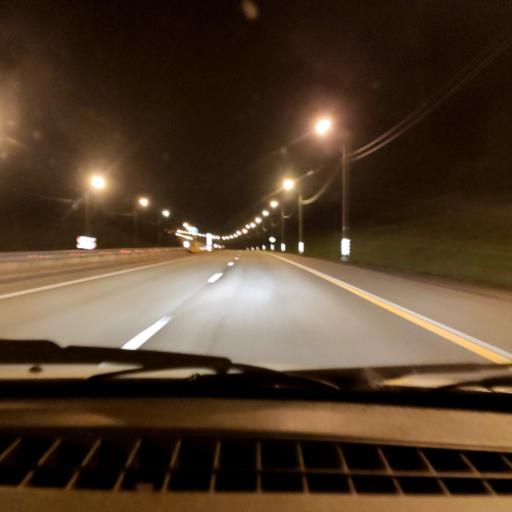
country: RU
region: Lipetsk
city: Zadonsk
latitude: 52.4001
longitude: 38.8595
